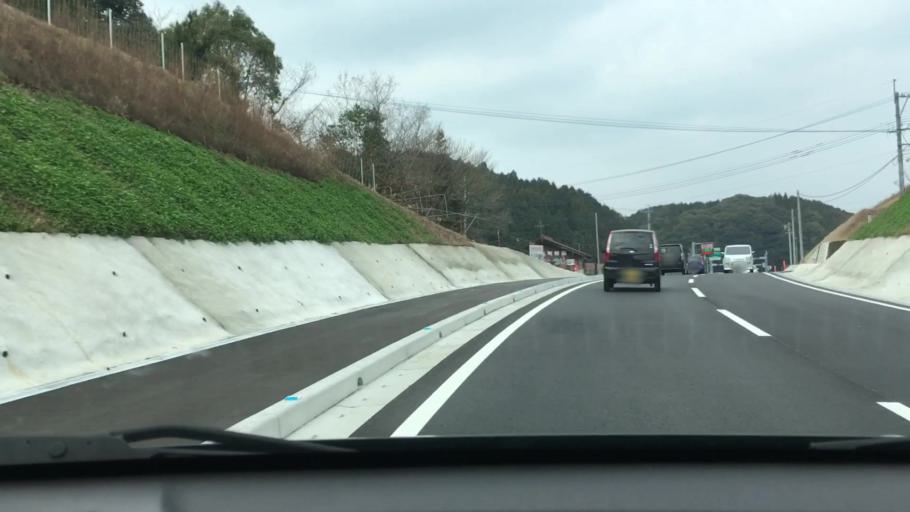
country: JP
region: Saga Prefecture
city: Imaricho-ko
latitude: 33.3404
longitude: 129.9216
